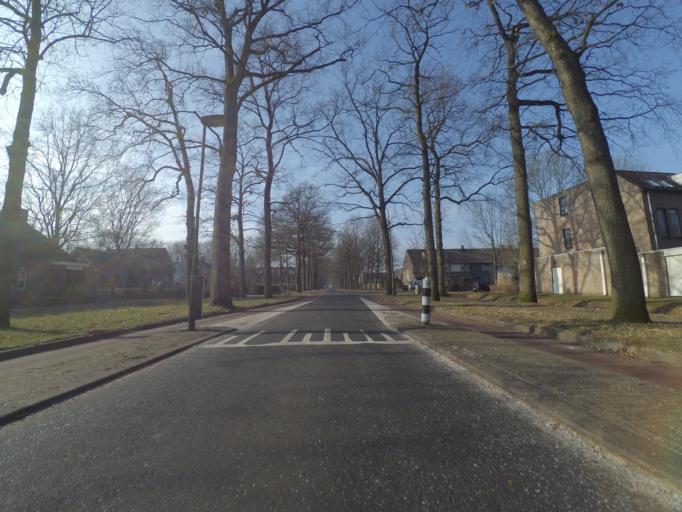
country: NL
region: Utrecht
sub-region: Gemeente Utrechtse Heuvelrug
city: Driebergen-Rijsenburg
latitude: 52.0501
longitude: 5.2666
